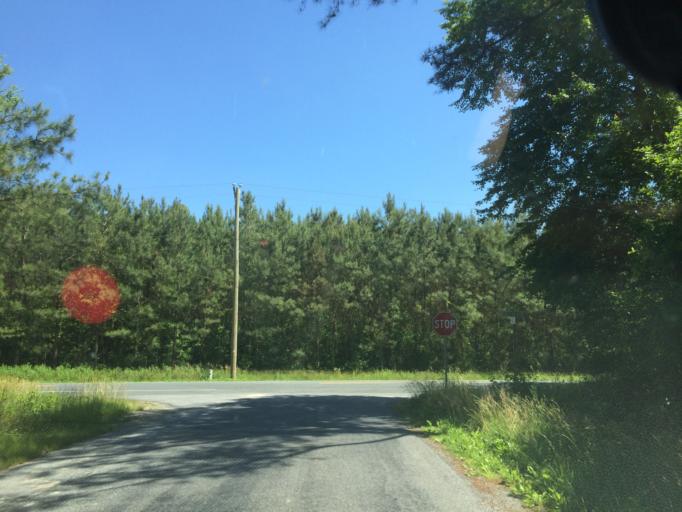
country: US
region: Maryland
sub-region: Wicomico County
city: Hebron
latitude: 38.3792
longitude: -75.7395
